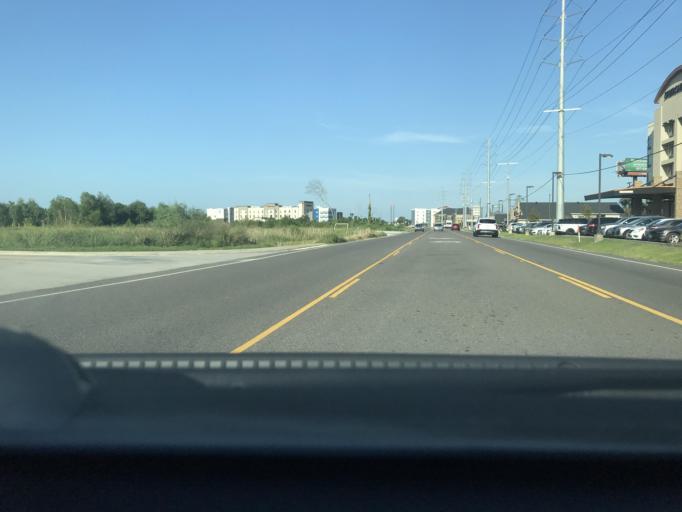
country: US
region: Louisiana
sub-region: Calcasieu Parish
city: Prien
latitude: 30.1977
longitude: -93.2447
